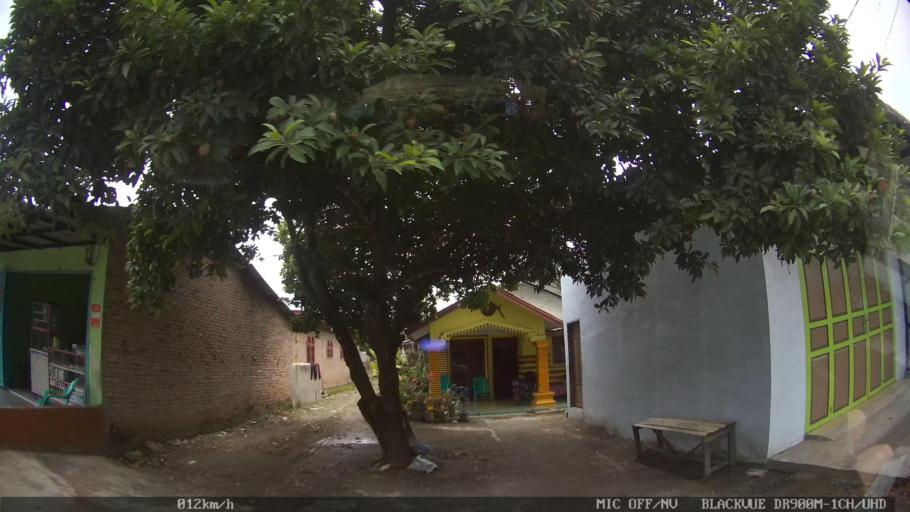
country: ID
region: North Sumatra
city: Sunggal
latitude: 3.6283
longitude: 98.5906
